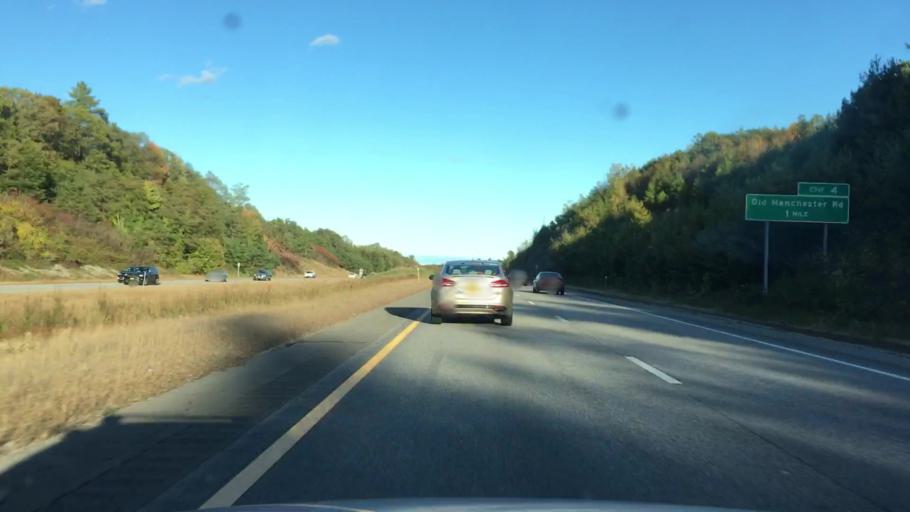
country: US
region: New Hampshire
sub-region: Rockingham County
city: Raymond
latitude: 43.0220
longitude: -71.2221
